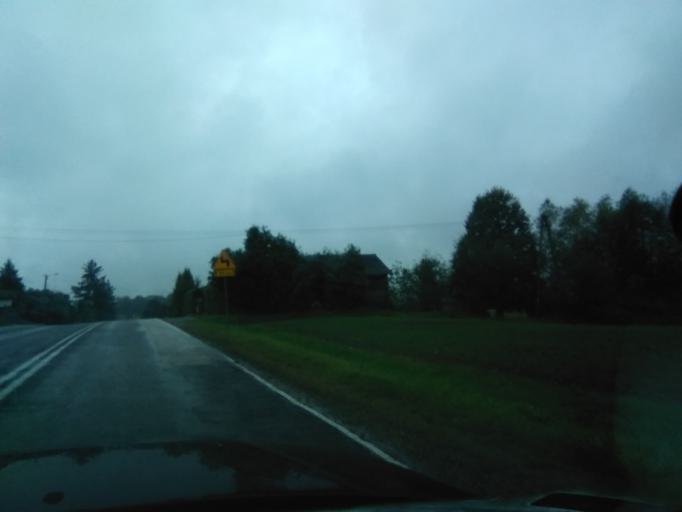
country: PL
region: Subcarpathian Voivodeship
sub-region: Powiat ropczycko-sedziszowski
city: Niedzwiada
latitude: 49.9969
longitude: 21.5634
